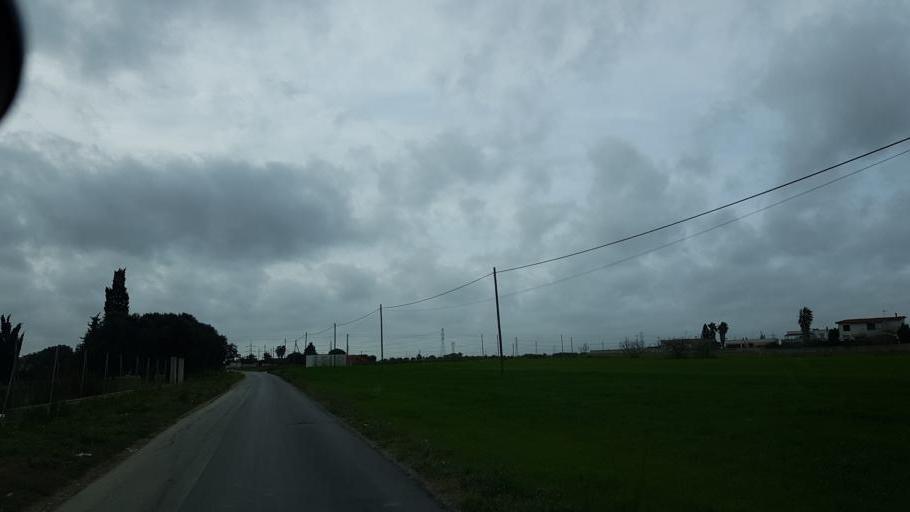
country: IT
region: Apulia
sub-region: Provincia di Brindisi
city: Brindisi
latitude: 40.6092
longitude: 17.9260
